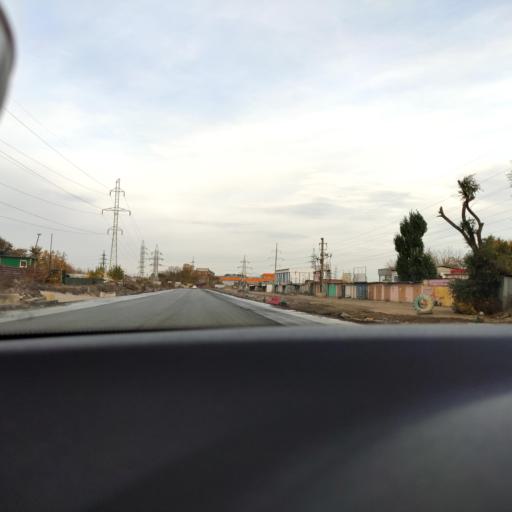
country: RU
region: Samara
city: Samara
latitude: 53.1927
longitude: 50.2296
